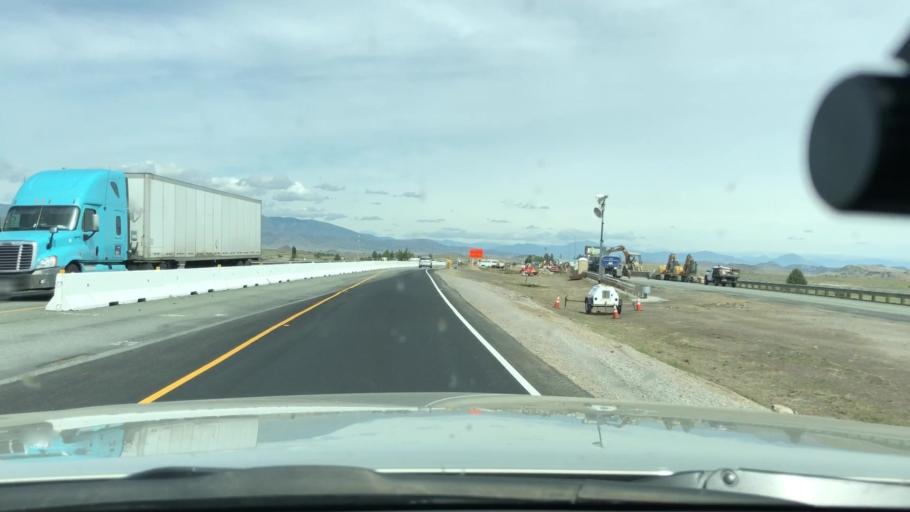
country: US
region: California
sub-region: Siskiyou County
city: Weed
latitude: 41.4700
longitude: -122.4509
